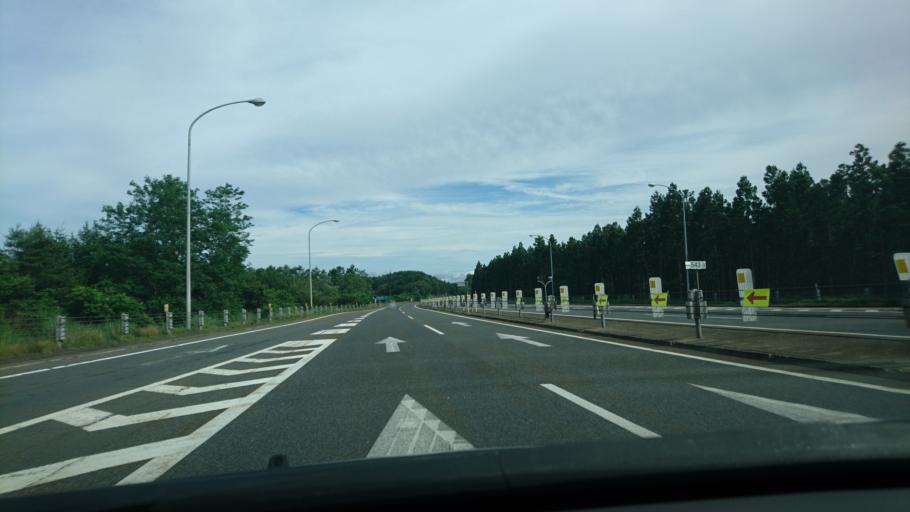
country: JP
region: Iwate
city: Shizukuishi
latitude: 39.9692
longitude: 141.0271
